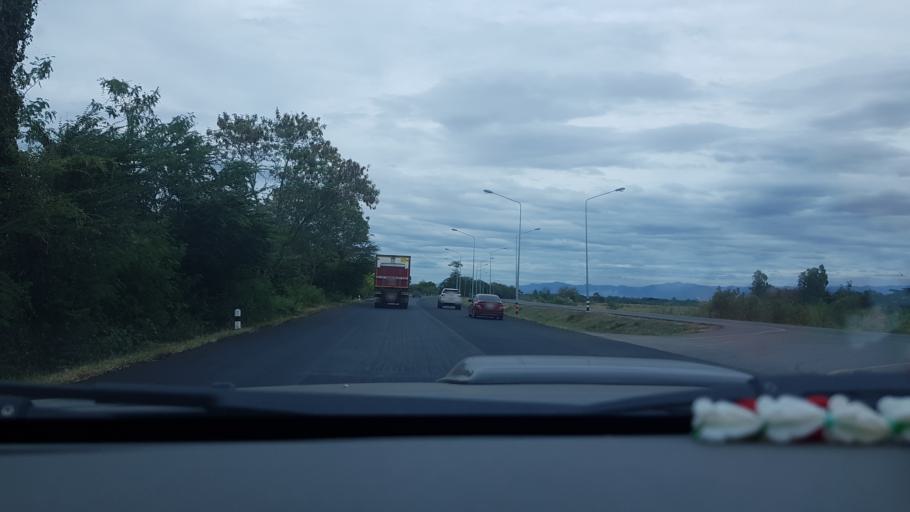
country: TH
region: Phetchabun
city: Phetchabun
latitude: 16.4906
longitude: 101.1416
